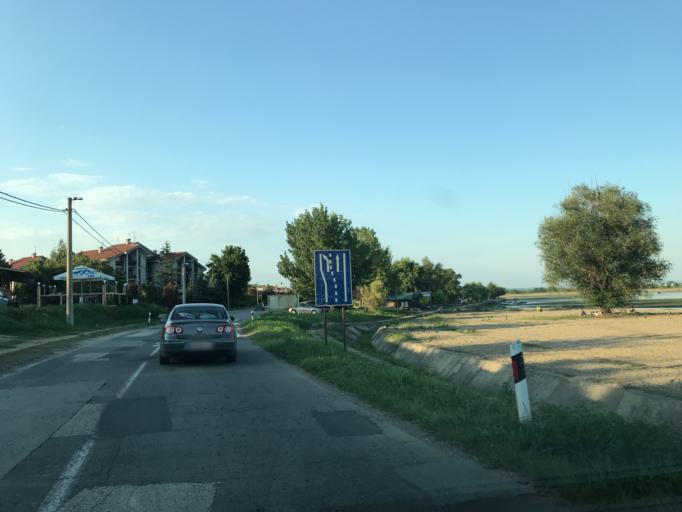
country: RO
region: Mehedinti
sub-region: Comuna Gogosu
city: Ostrovu Mare
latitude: 44.4810
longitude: 22.4538
